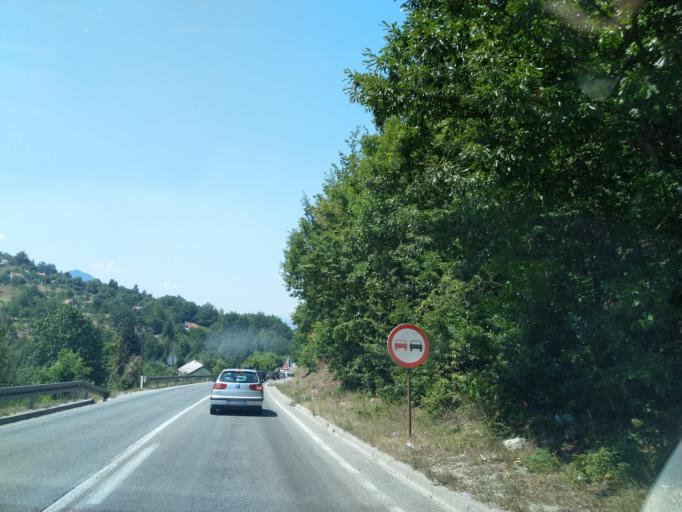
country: RS
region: Central Serbia
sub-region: Zlatiborski Okrug
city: Nova Varos
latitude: 43.4609
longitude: 19.7689
